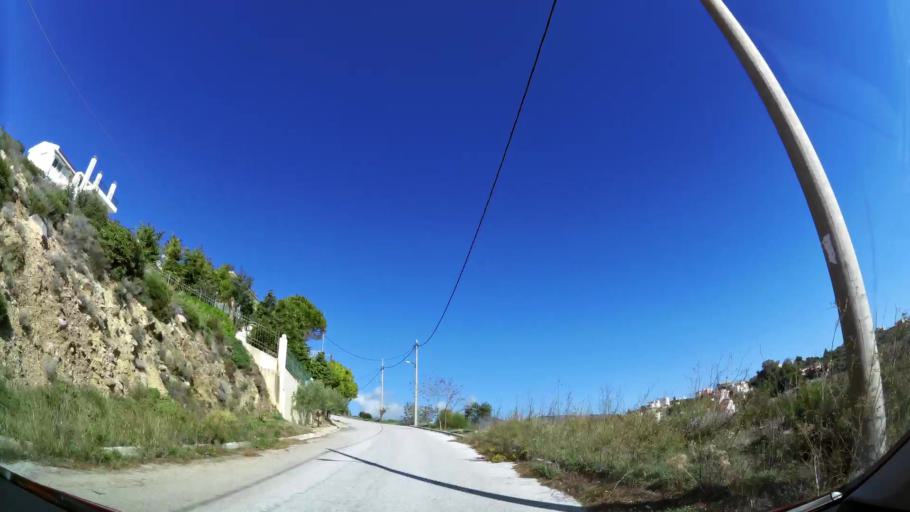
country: GR
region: Attica
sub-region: Nomarchia Anatolikis Attikis
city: Dhrafi
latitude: 38.0212
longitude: 23.8983
